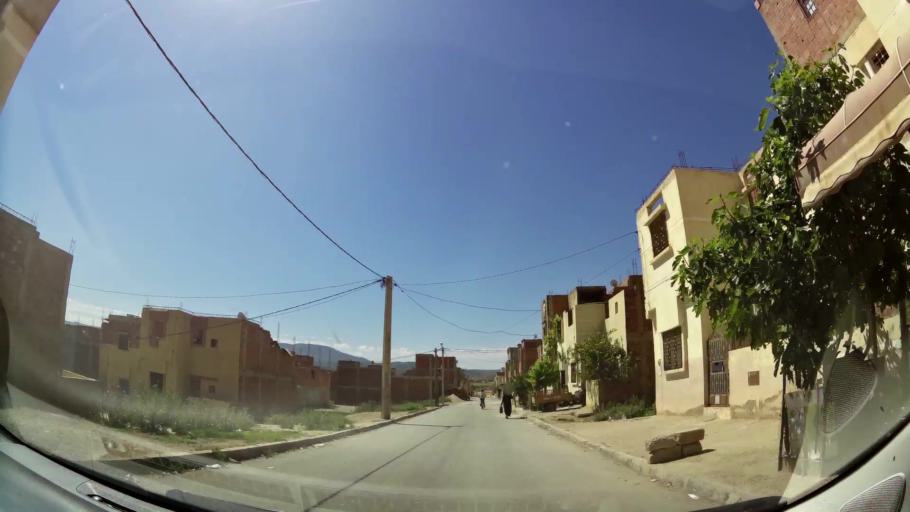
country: MA
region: Oriental
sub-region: Oujda-Angad
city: Oujda
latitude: 34.6530
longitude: -1.8682
